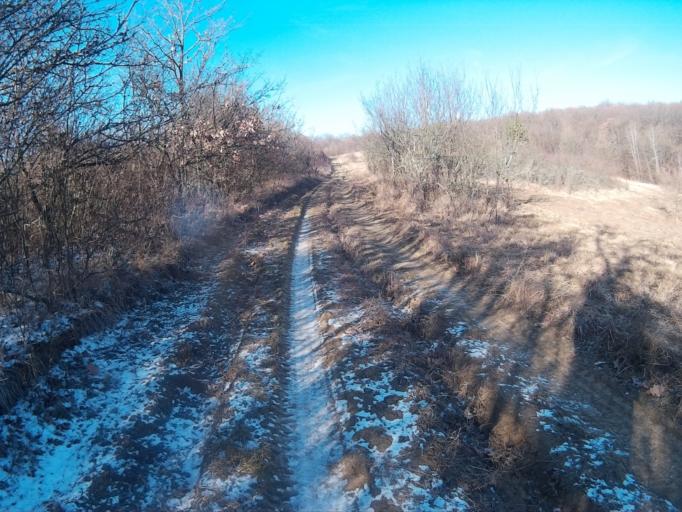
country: HU
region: Borsod-Abauj-Zemplen
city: Putnok
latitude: 48.4048
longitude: 20.4838
